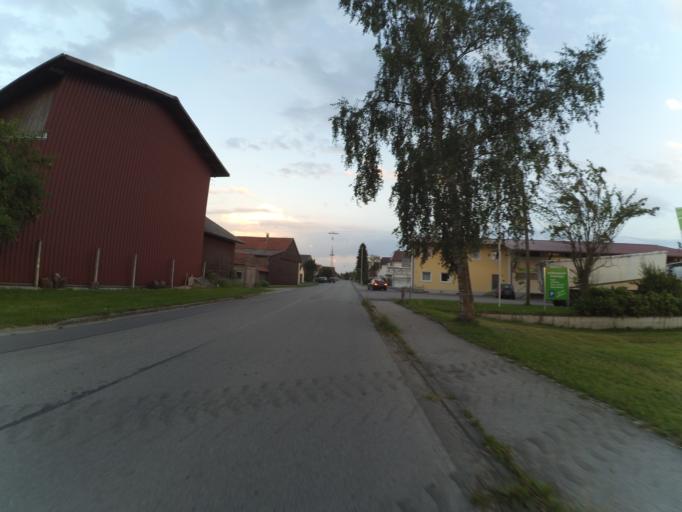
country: DE
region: Bavaria
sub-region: Swabia
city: Tussenhausen
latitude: 48.0656
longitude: 10.5811
